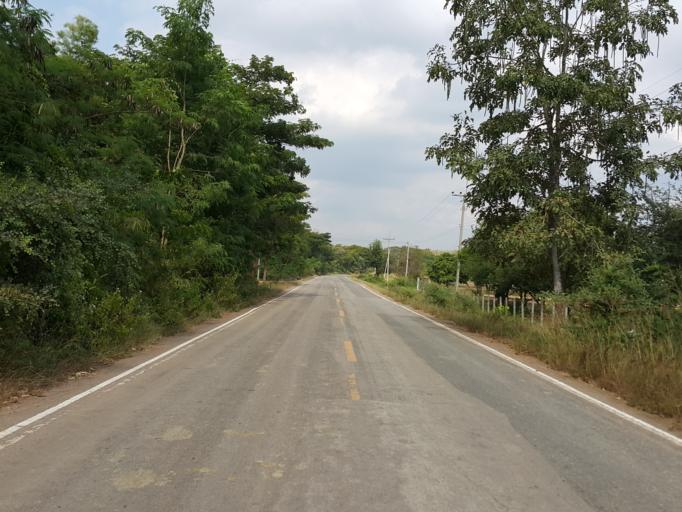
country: TH
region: Sukhothai
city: Thung Saliam
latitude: 17.3582
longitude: 99.5936
